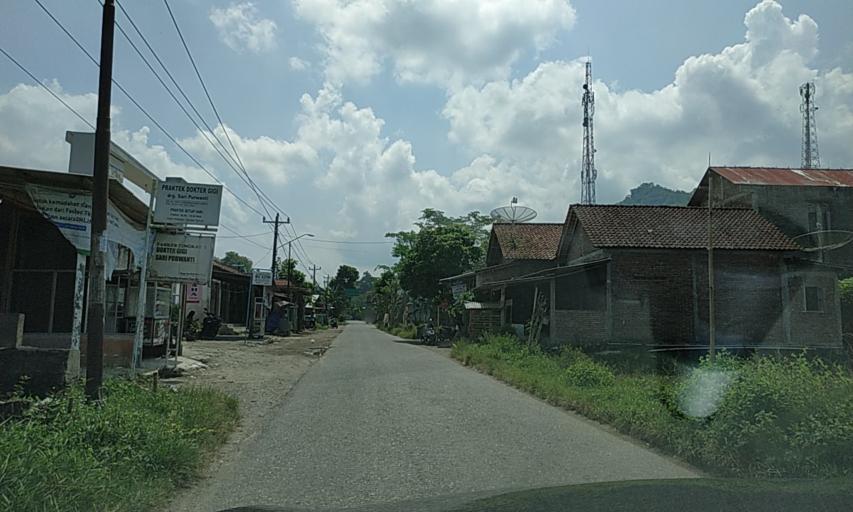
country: ID
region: Central Java
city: Gombong
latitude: -7.6350
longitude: 109.7073
